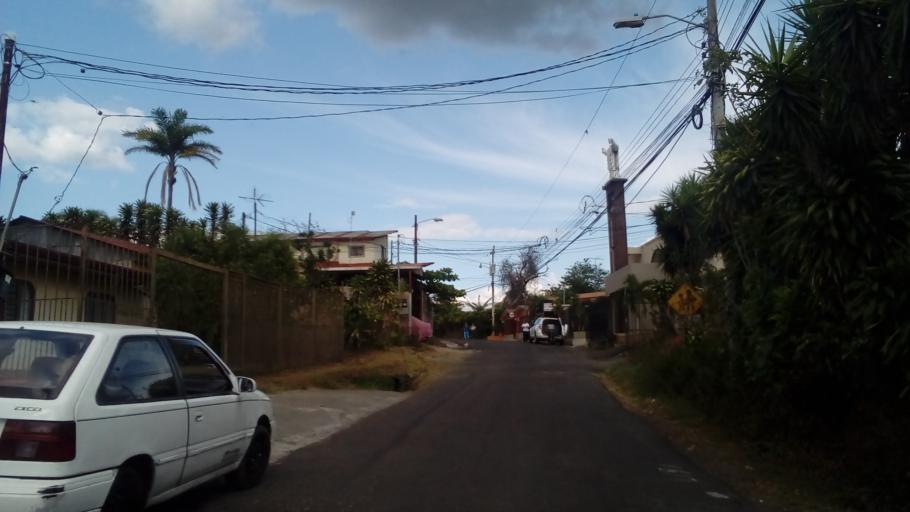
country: CR
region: Alajuela
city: San Juan
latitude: 10.0957
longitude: -84.2813
